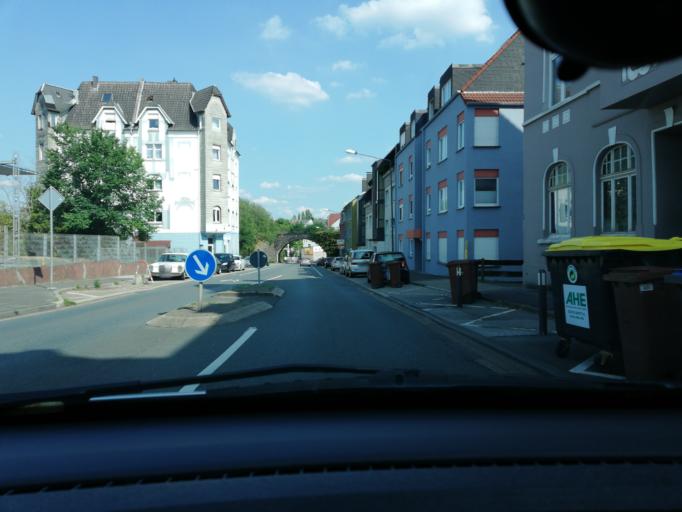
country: DE
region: North Rhine-Westphalia
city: Gevelsberg
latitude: 51.3200
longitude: 7.3188
